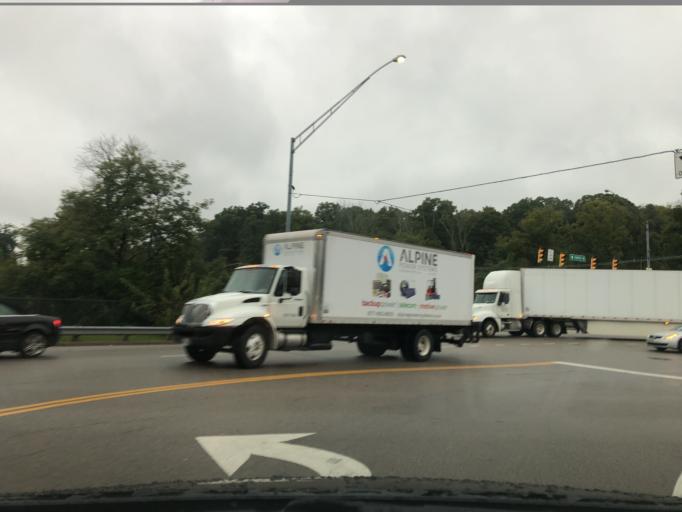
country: US
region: Ohio
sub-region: Hamilton County
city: Highpoint
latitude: 39.2818
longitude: -84.3717
